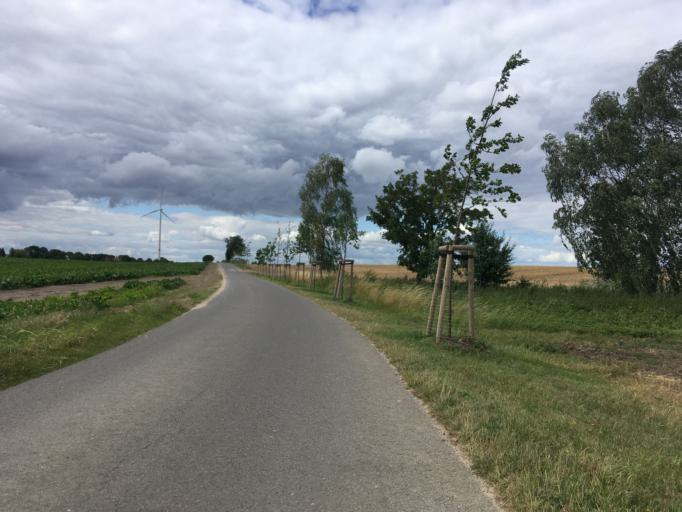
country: DE
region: Brandenburg
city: Gramzow
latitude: 53.2654
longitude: 14.0163
